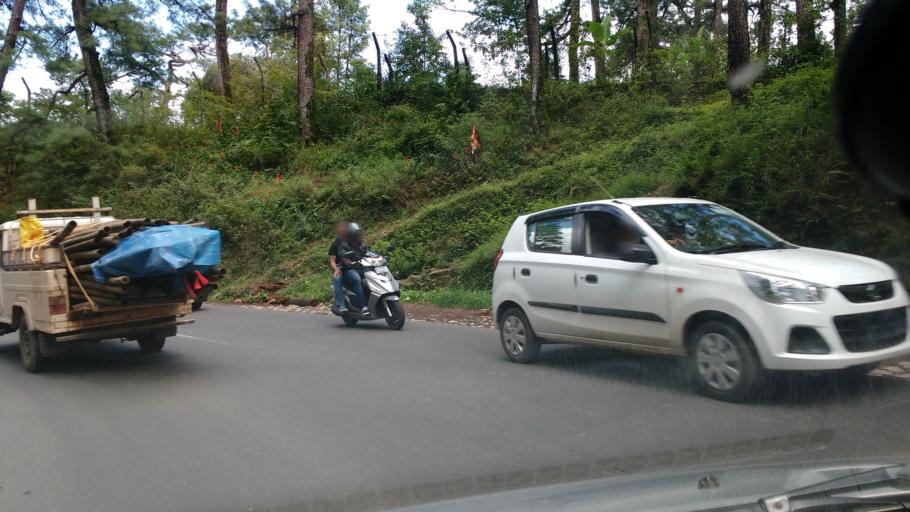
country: IN
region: Meghalaya
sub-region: East Khasi Hills
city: Shillong
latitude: 25.5651
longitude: 91.8590
